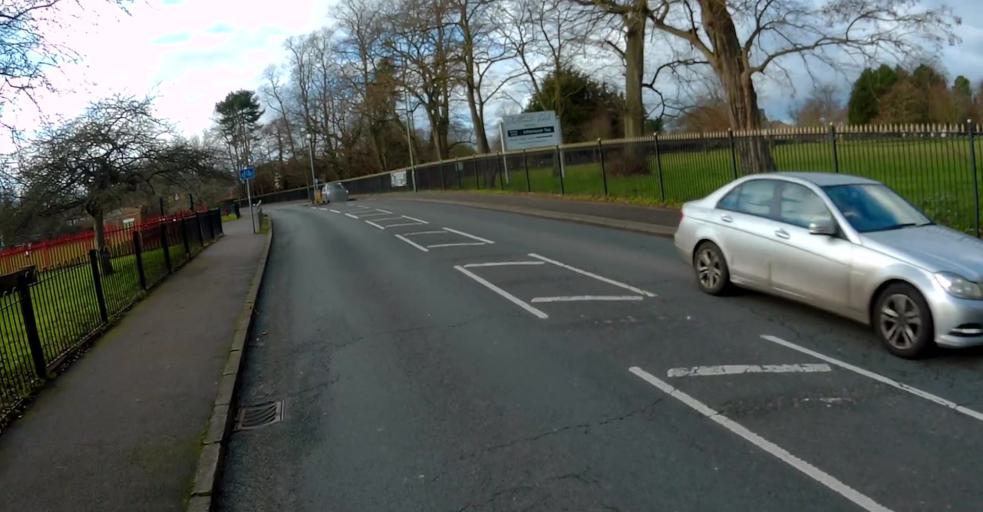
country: GB
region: England
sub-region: Surrey
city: Weybridge
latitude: 51.3728
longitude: -0.4421
